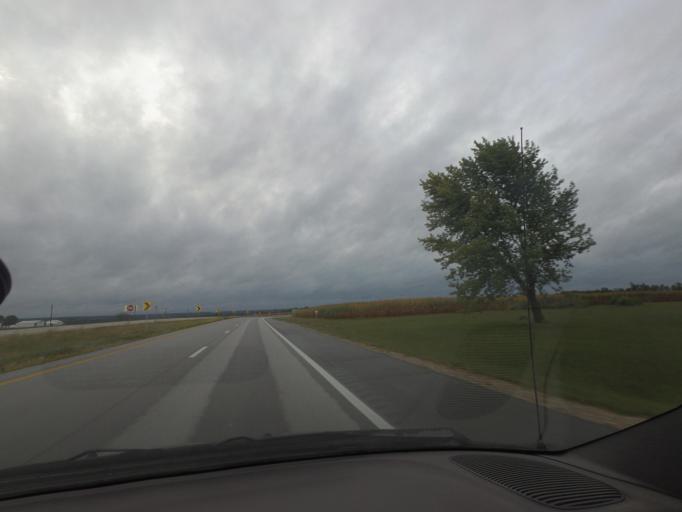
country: US
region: Missouri
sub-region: Shelby County
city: Shelbina
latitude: 39.6744
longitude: -91.9498
